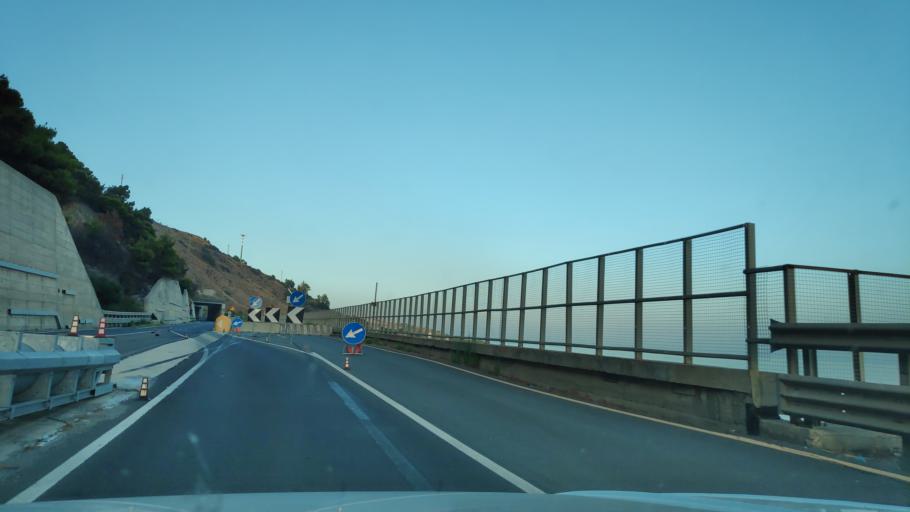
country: IT
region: Calabria
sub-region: Provincia di Reggio Calabria
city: Palizzi Marina
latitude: 37.9200
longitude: 15.9674
